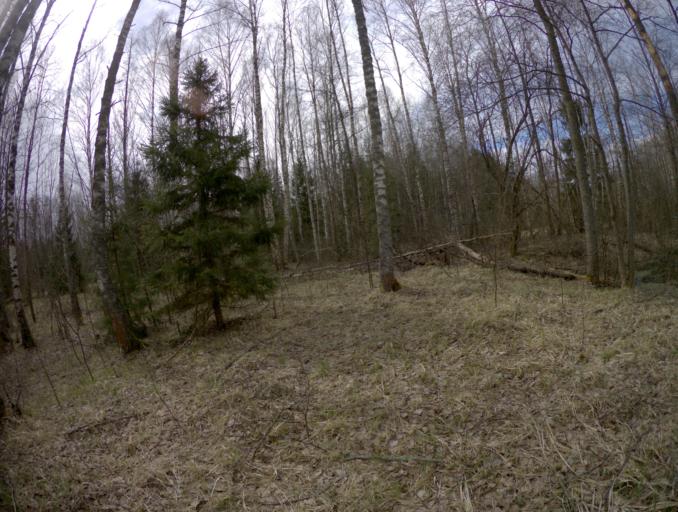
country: RU
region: Vladimir
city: Raduzhnyy
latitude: 55.8780
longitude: 40.2081
